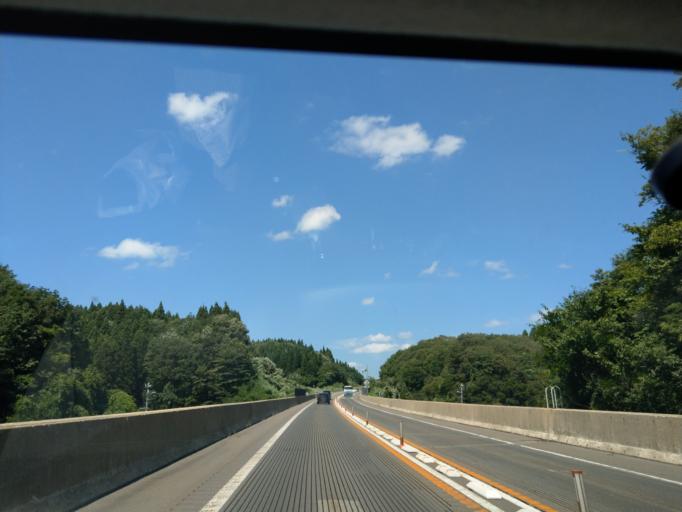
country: JP
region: Akita
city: Akita
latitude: 39.6774
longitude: 140.1859
